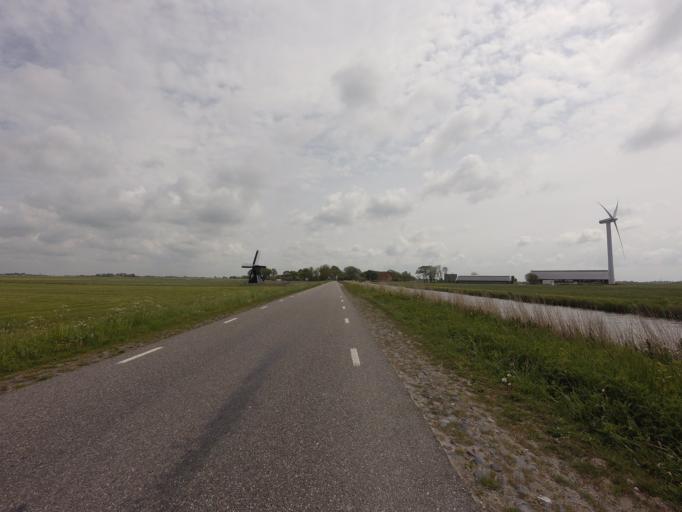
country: NL
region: Friesland
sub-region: Sudwest Fryslan
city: Bolsward
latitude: 53.1001
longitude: 5.5174
